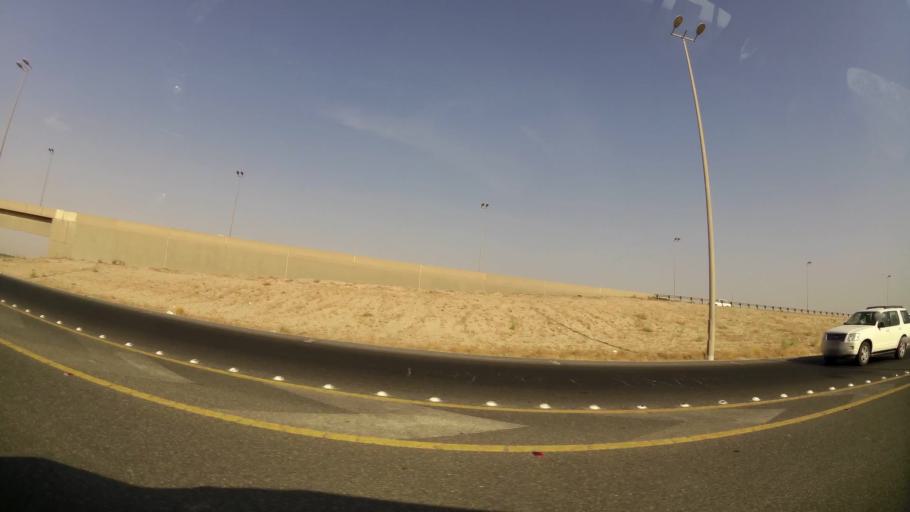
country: KW
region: Al Farwaniyah
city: Janub as Surrah
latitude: 29.1843
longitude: 47.9946
